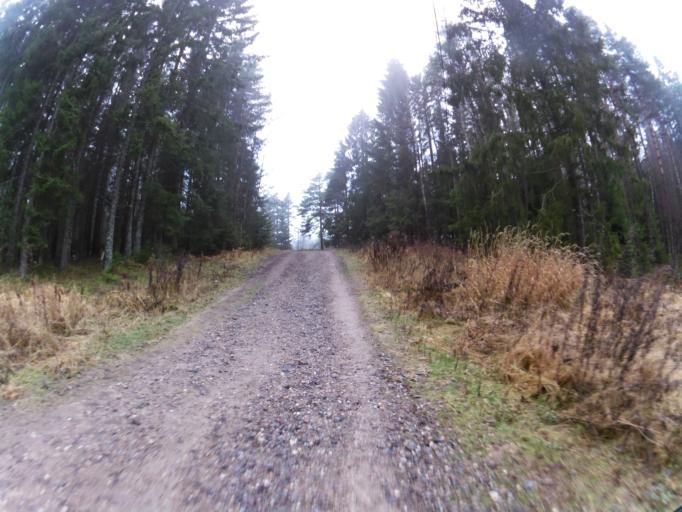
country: NO
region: Ostfold
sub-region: Fredrikstad
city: Fredrikstad
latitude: 59.2673
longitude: 10.9830
